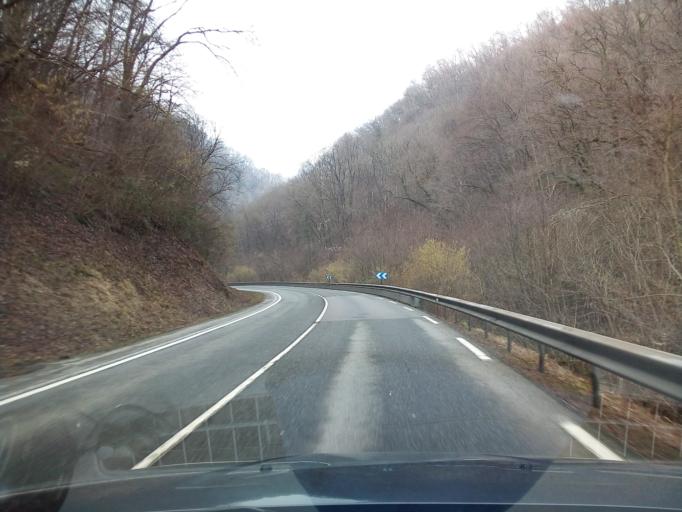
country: FR
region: Rhone-Alpes
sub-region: Departement de l'Isere
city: Gieres
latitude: 45.1653
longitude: 5.8035
